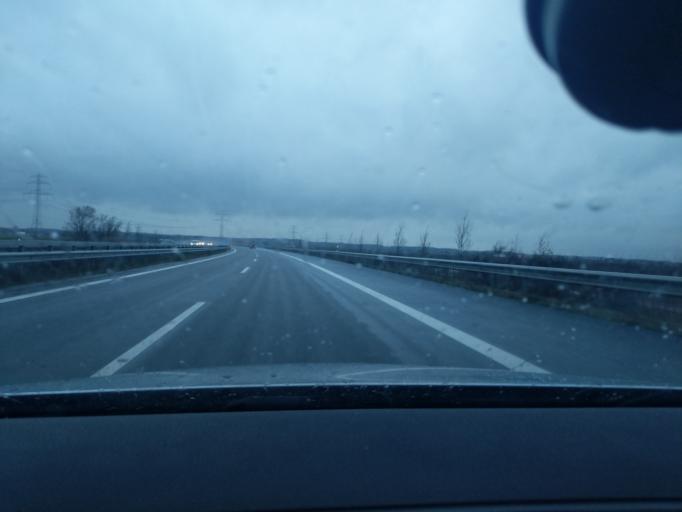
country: DE
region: Lower Saxony
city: Neuenkirchen
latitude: 53.5119
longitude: 9.6216
